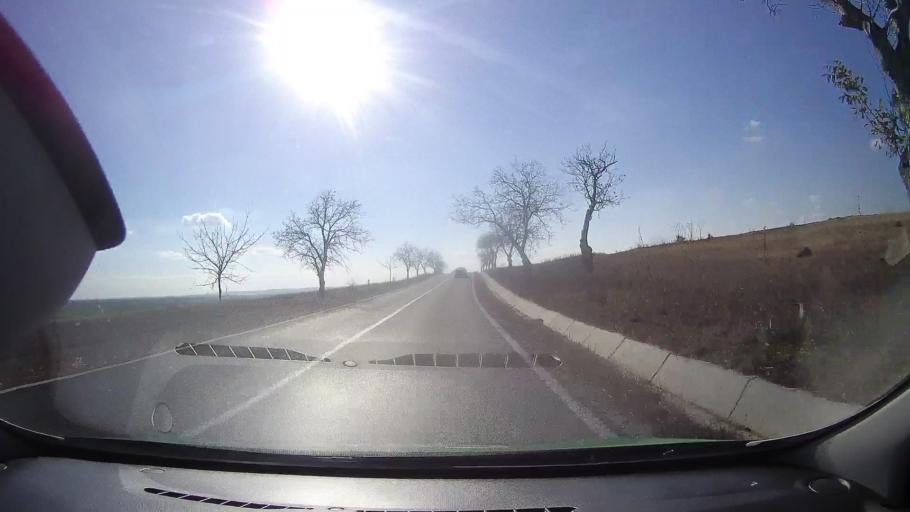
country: RO
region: Tulcea
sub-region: Comuna Ceamurlia de Jos
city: Ceamurlia de Jos
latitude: 44.8081
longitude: 28.6912
